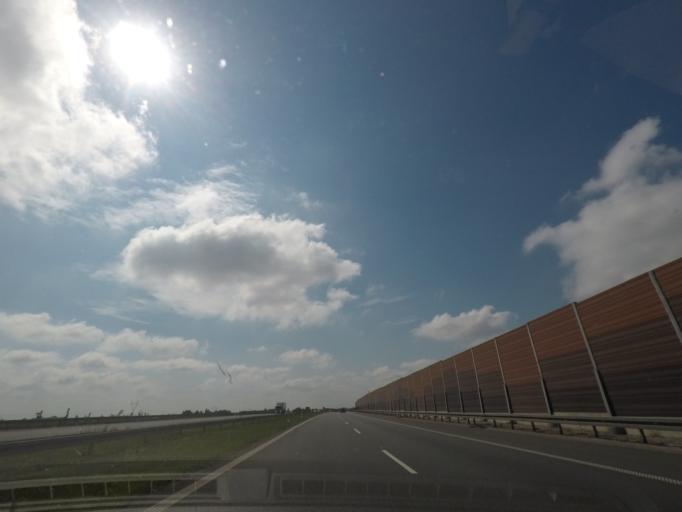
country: PL
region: Kujawsko-Pomorskie
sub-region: Powiat aleksandrowski
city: Waganiec
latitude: 52.7553
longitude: 18.8585
